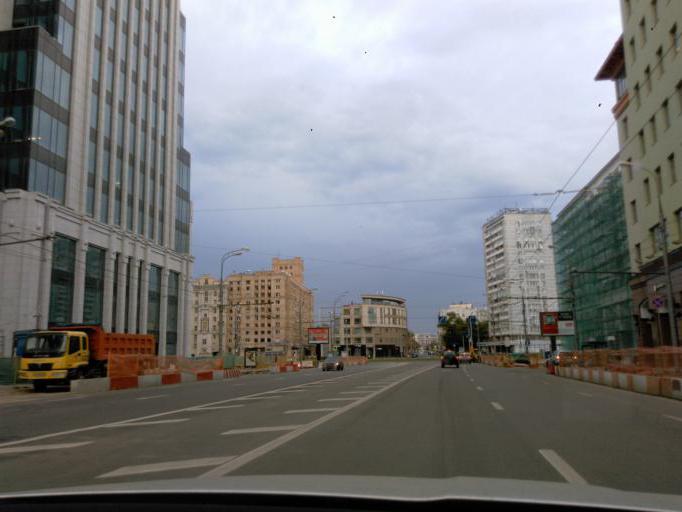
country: RU
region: Moscow
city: Moscow
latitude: 55.7742
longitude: 37.6039
